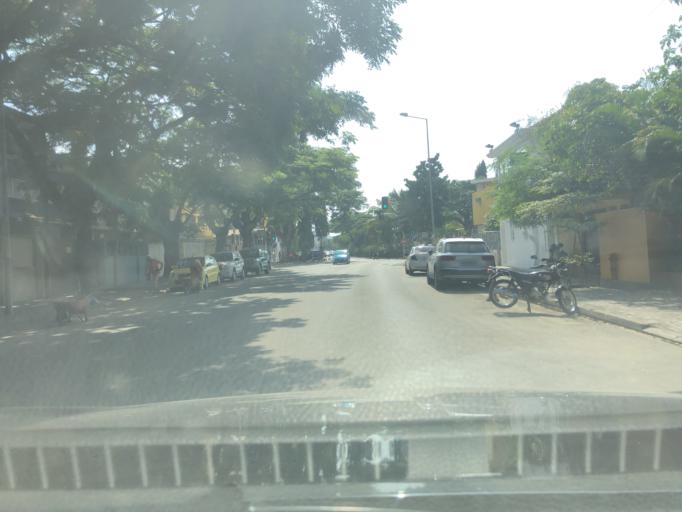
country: AO
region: Luanda
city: Luanda
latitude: -8.8271
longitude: 13.2491
